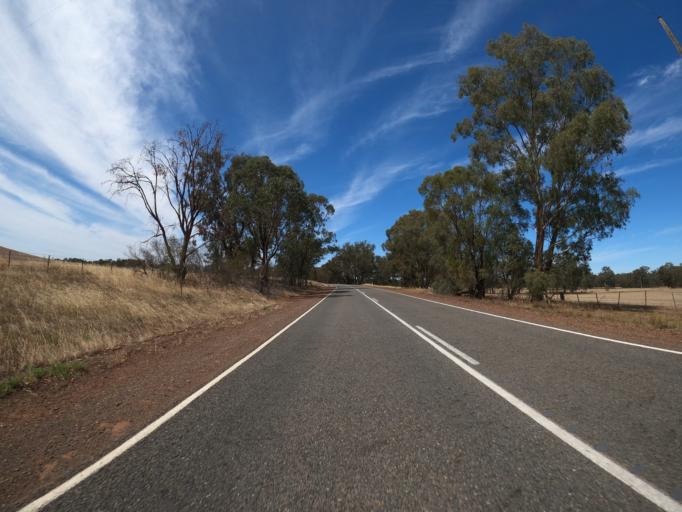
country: AU
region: Victoria
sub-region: Benalla
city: Benalla
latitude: -36.3414
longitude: 145.9590
